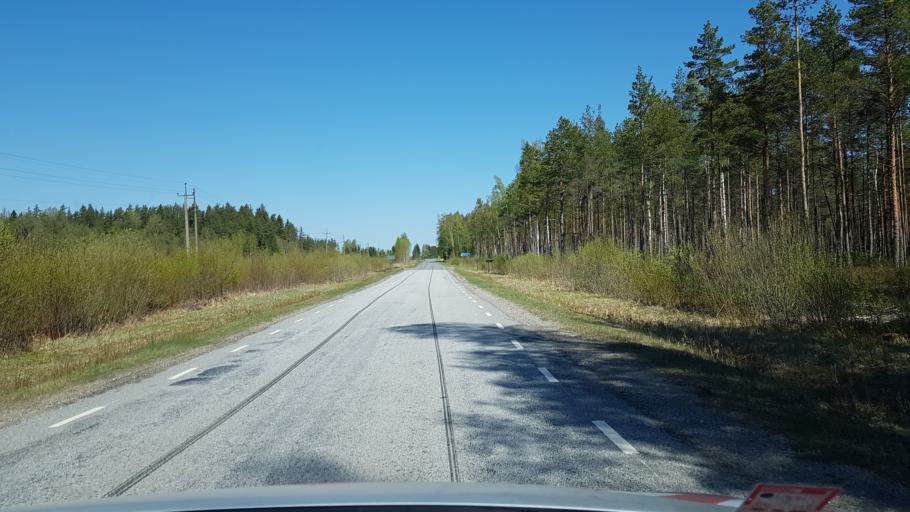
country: EE
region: Vorumaa
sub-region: Voru linn
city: Voru
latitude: 57.9356
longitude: 26.9524
